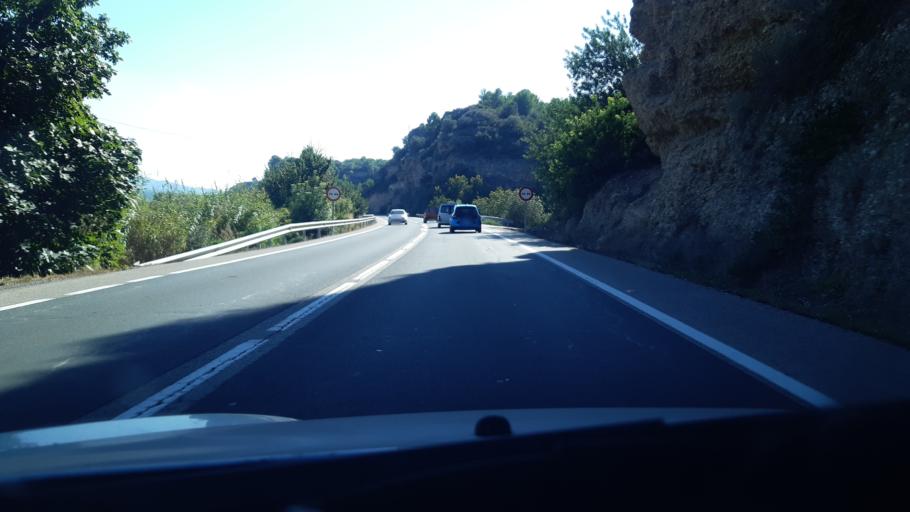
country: ES
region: Catalonia
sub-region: Provincia de Tarragona
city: Tivenys
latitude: 40.8723
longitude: 0.5013
